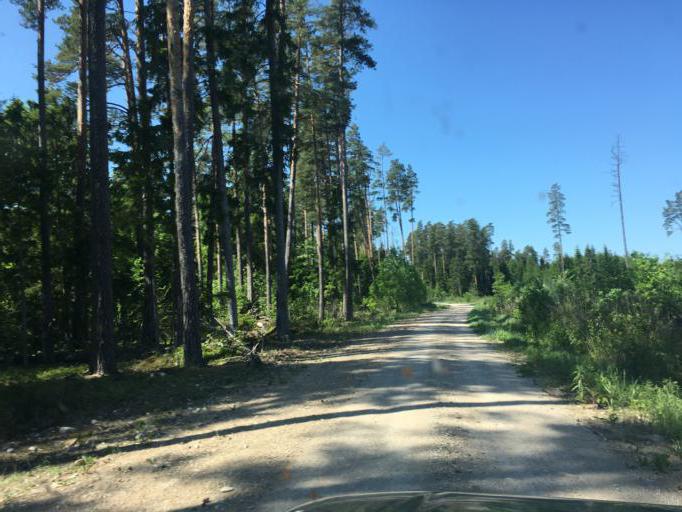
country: LV
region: Talsu Rajons
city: Valdemarpils
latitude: 57.4375
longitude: 22.6795
